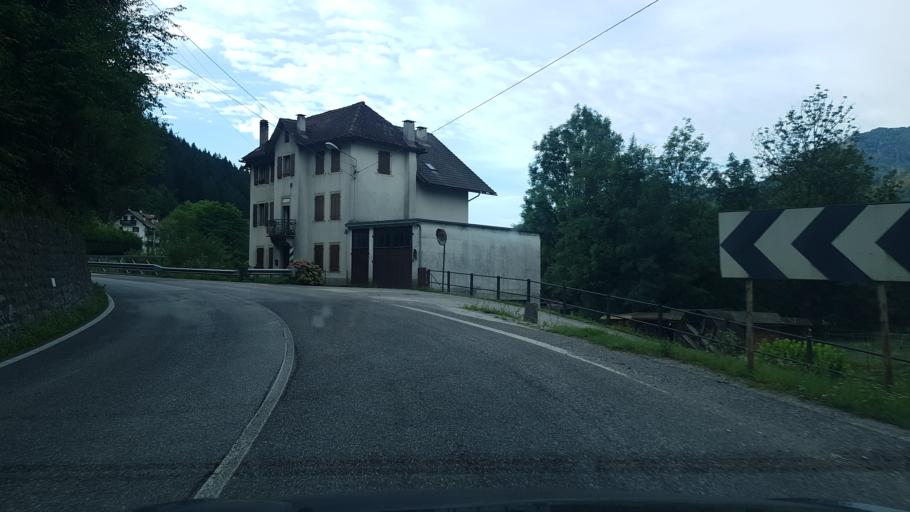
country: IT
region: Friuli Venezia Giulia
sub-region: Provincia di Udine
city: Ovaro
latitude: 46.4999
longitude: 12.8653
